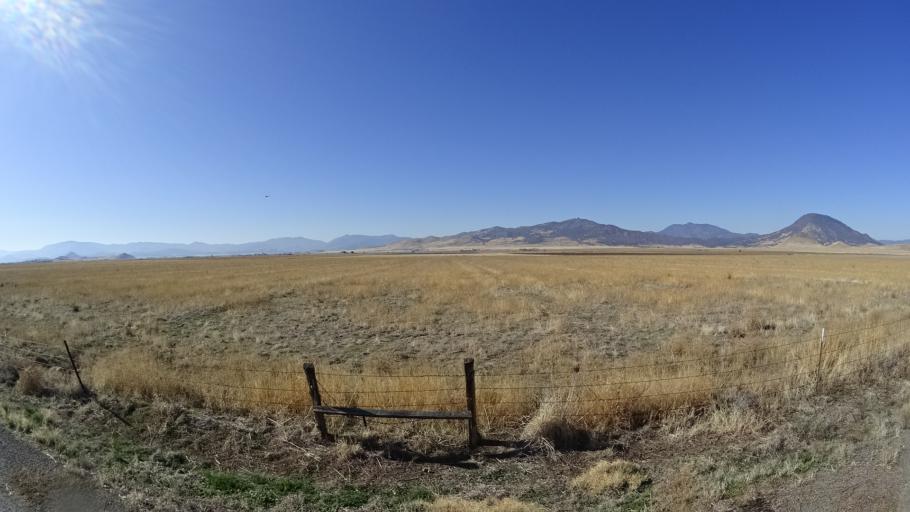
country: US
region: California
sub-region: Siskiyou County
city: Montague
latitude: 41.7889
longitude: -122.4344
